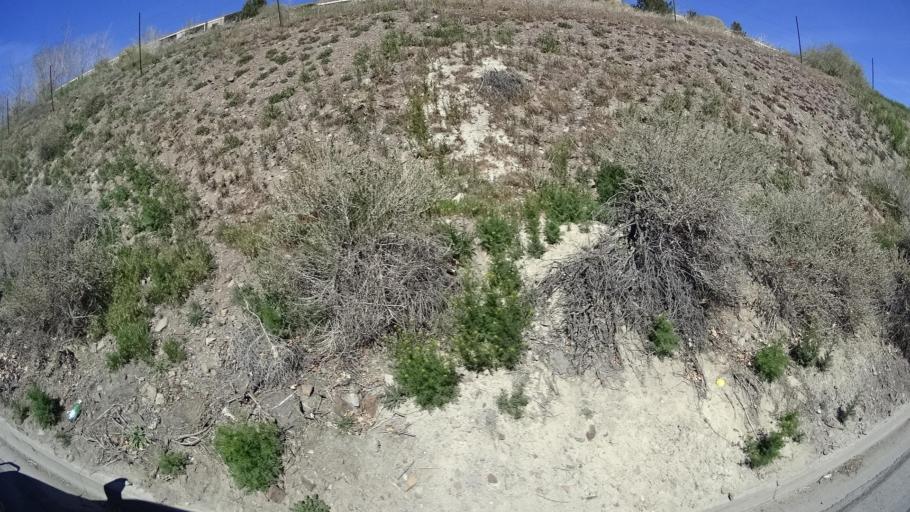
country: US
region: Nevada
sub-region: Washoe County
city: Reno
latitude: 39.5512
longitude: -119.7850
